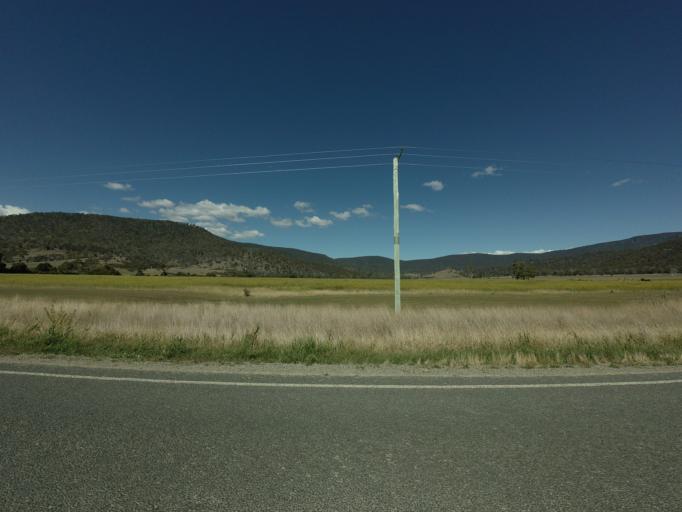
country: AU
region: Tasmania
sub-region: Break O'Day
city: St Helens
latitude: -41.6718
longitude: 147.9002
